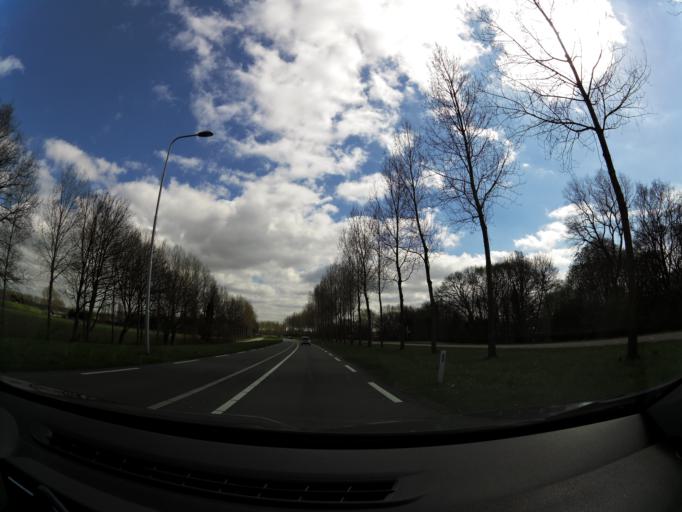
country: NL
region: South Holland
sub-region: Gemeente Brielle
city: Brielle
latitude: 51.9209
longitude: 4.1050
